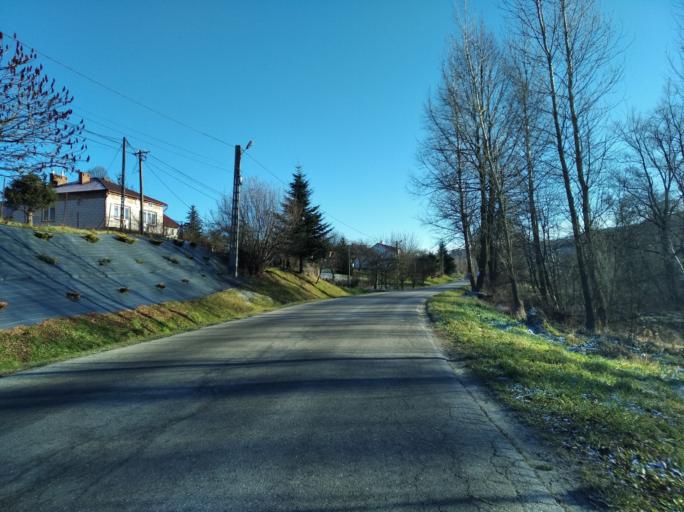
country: PL
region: Subcarpathian Voivodeship
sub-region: Powiat strzyzowski
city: Strzyzow
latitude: 49.9275
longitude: 21.7799
